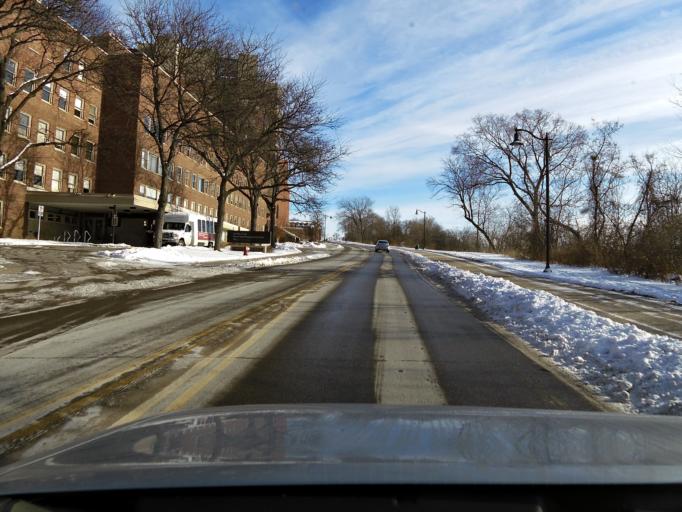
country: US
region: Minnesota
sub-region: Hennepin County
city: Minneapolis
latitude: 44.9710
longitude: -93.2340
